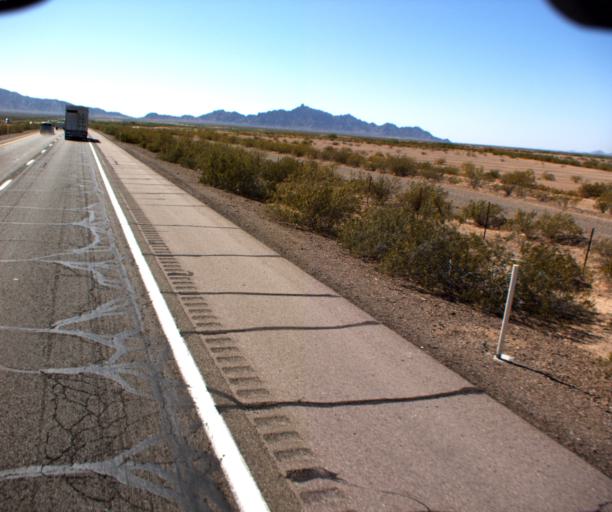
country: US
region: Arizona
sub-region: Yuma County
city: Wellton
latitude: 32.7591
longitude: -113.6404
